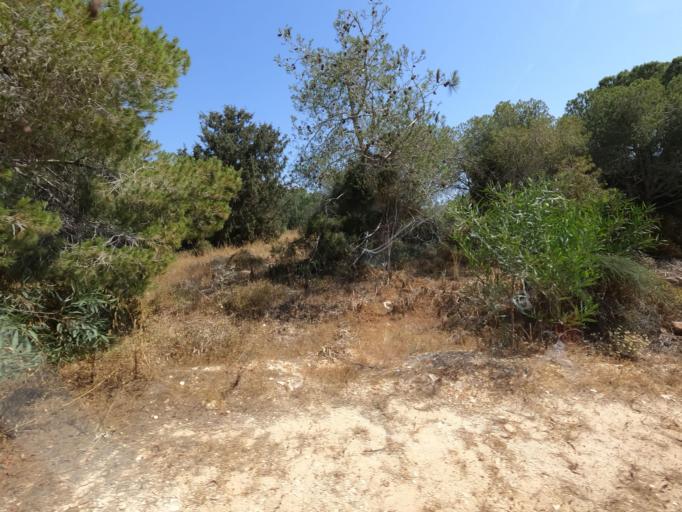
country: CY
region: Ammochostos
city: Paralimni
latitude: 35.0030
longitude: 33.9693
